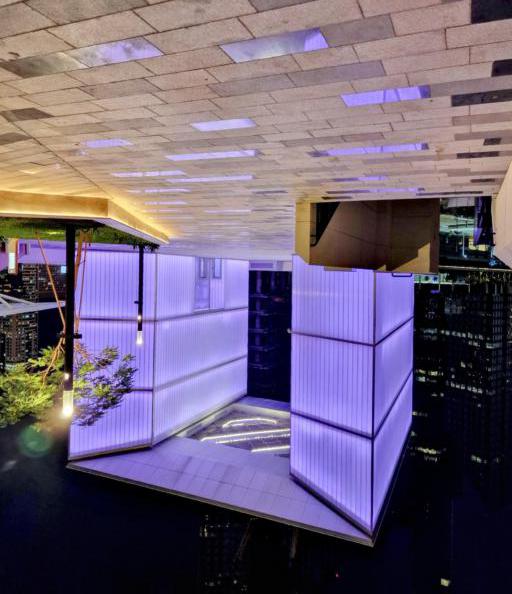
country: AE
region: Dubai
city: Dubai
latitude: 25.2080
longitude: 55.2768
